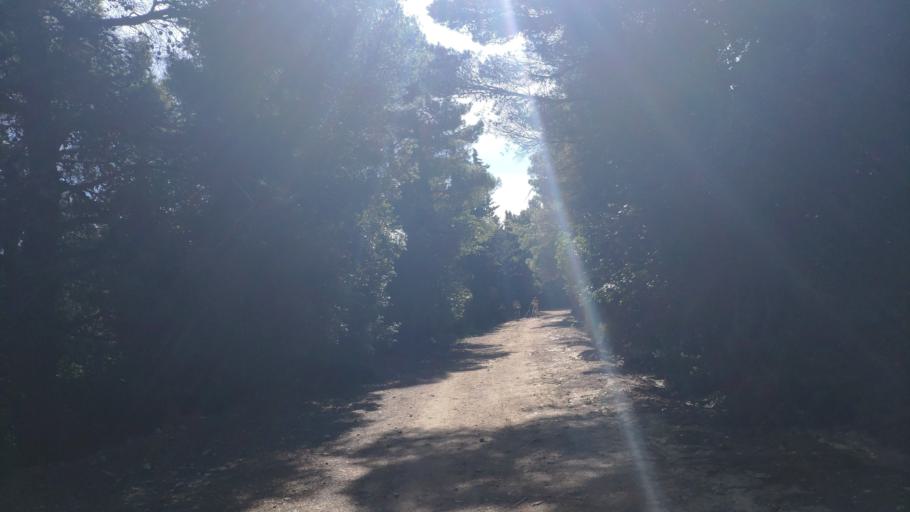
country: GR
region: Attica
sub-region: Nomarchia Anatolikis Attikis
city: Varybobi
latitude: 38.1578
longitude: 23.7767
